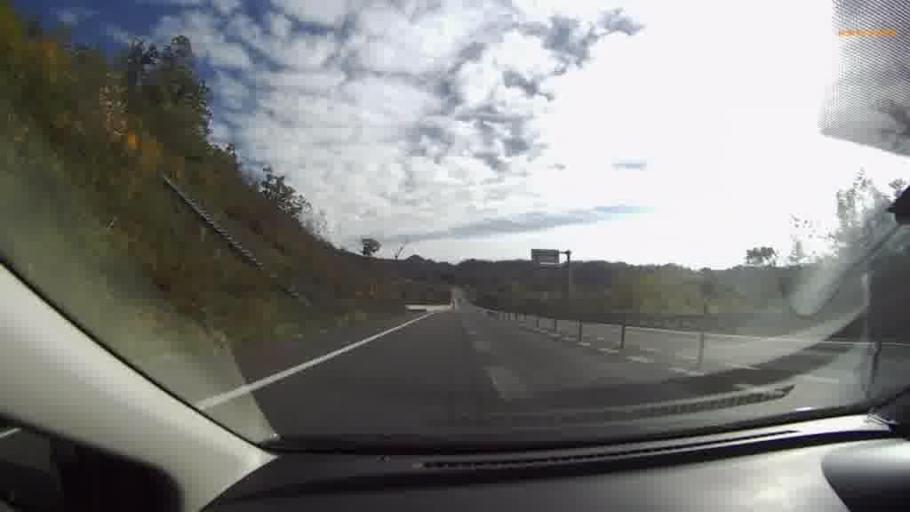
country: JP
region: Hokkaido
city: Kushiro
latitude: 43.0795
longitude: 143.9644
